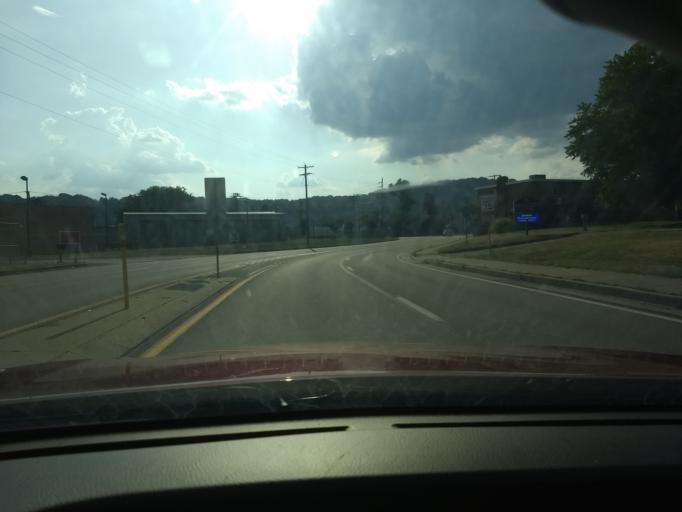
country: US
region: Pennsylvania
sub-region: Westmoreland County
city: Lower Burrell
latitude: 40.5529
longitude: -79.7592
